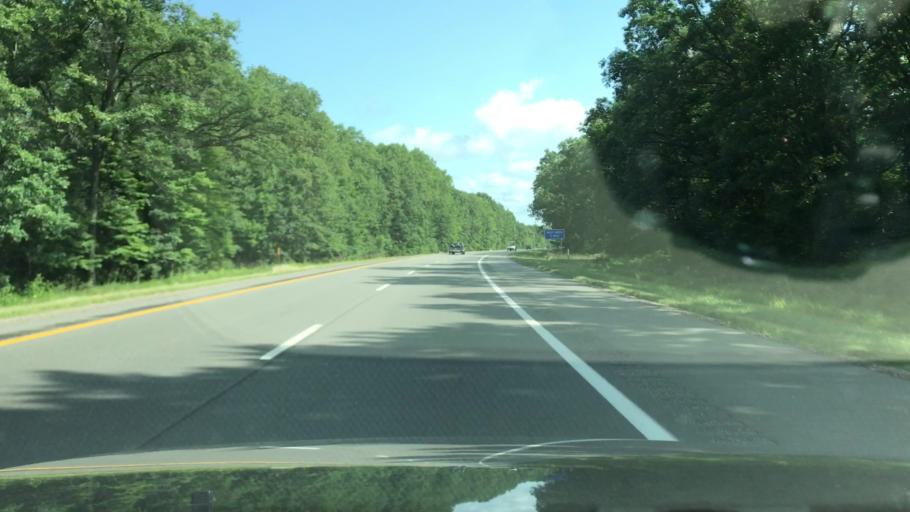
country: US
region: Michigan
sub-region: Montcalm County
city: Howard City
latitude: 43.4422
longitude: -85.4912
